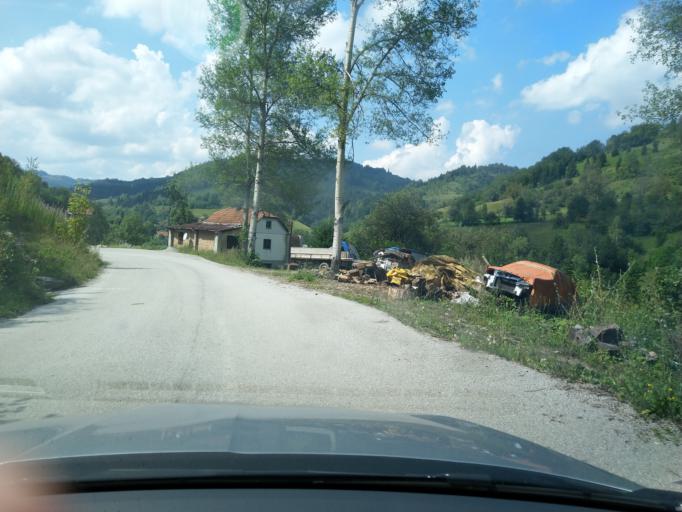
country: RS
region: Central Serbia
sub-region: Zlatiborski Okrug
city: Nova Varos
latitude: 43.5812
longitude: 19.8818
